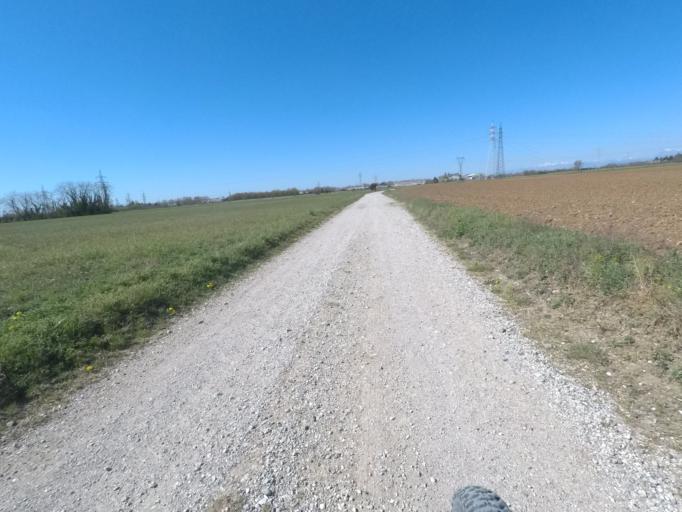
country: IT
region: Friuli Venezia Giulia
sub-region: Provincia di Udine
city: Remanzacco
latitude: 46.0888
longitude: 13.3072
